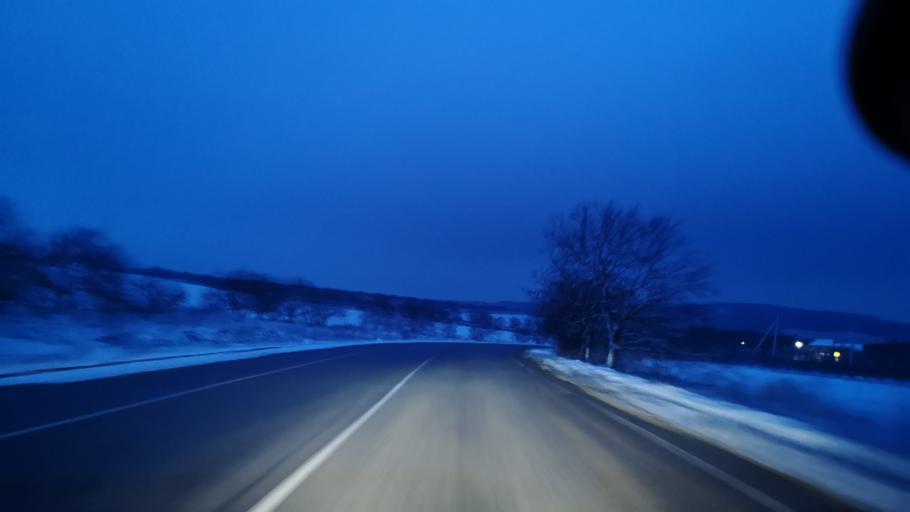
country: MD
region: Orhei
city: Orhei
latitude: 47.5241
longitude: 28.7973
